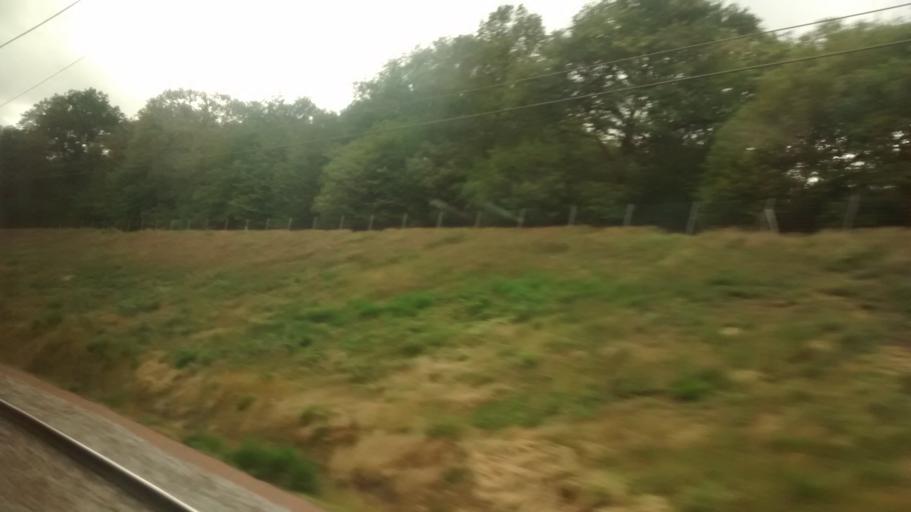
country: FR
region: Ile-de-France
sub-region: Departement des Yvelines
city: Saint-Arnoult-en-Yvelines
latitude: 48.5464
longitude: 1.9245
